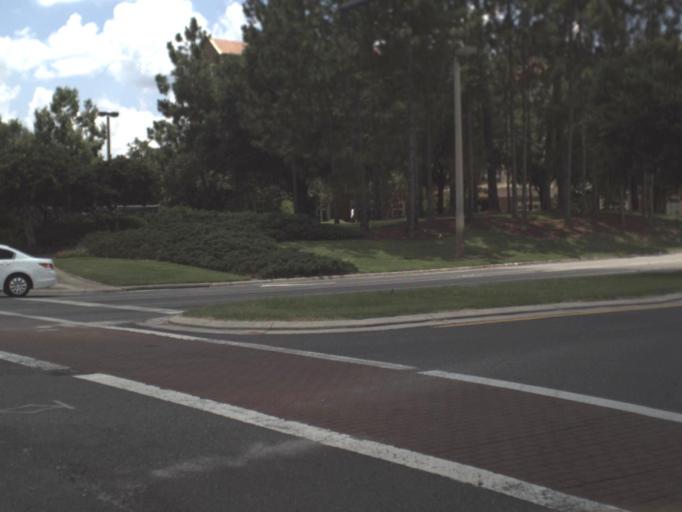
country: US
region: Florida
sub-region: Alachua County
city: Gainesville
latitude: 29.6378
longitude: -82.3726
